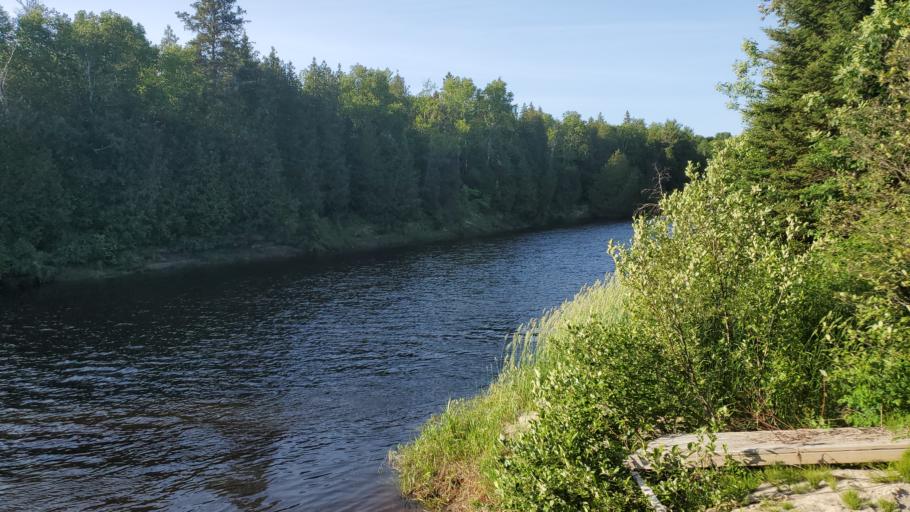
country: CA
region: Ontario
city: Rayside-Balfour
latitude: 46.5755
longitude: -81.3143
